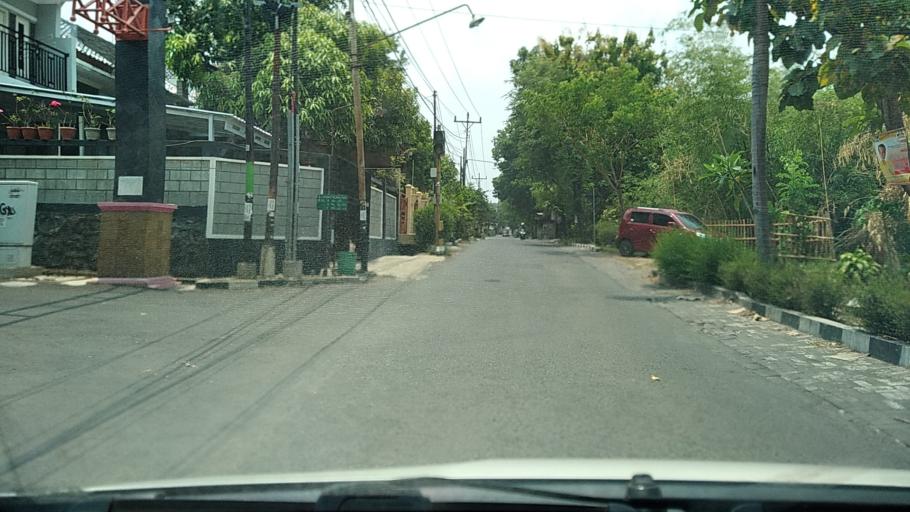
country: ID
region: Central Java
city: Semarang
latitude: -7.0046
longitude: 110.3690
